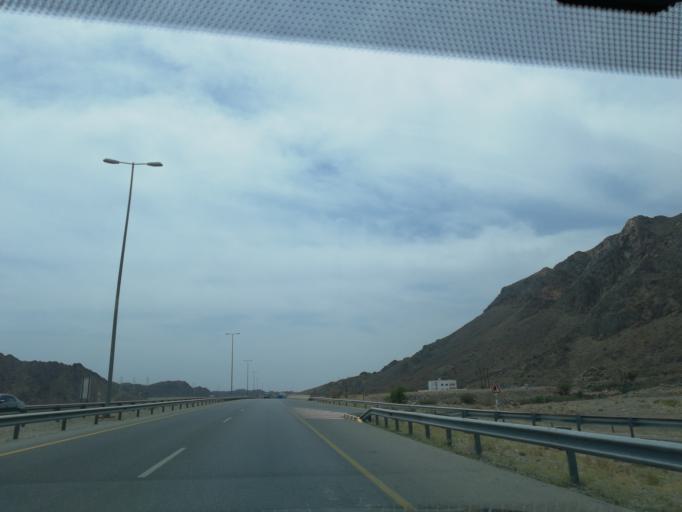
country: OM
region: Muhafazat ad Dakhiliyah
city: Izki
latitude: 23.1334
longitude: 57.8412
